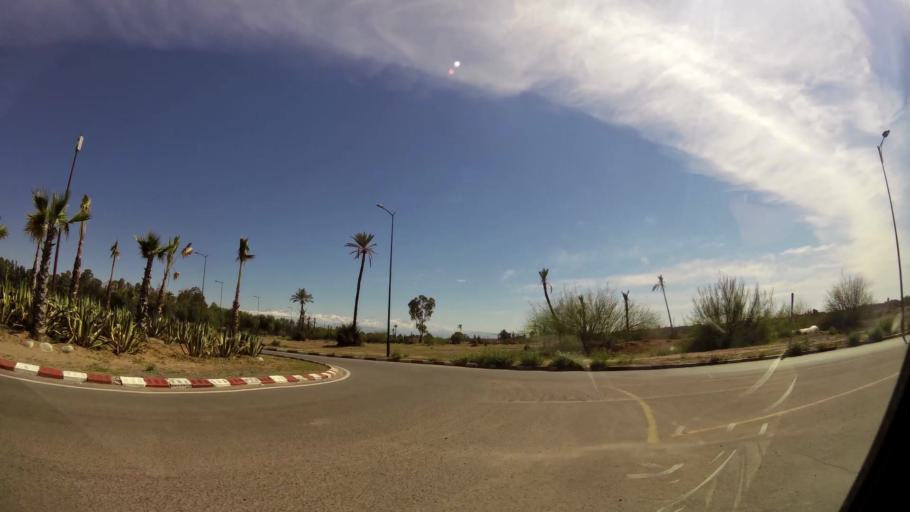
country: MA
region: Marrakech-Tensift-Al Haouz
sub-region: Marrakech
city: Marrakesh
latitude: 31.6170
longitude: -7.9545
